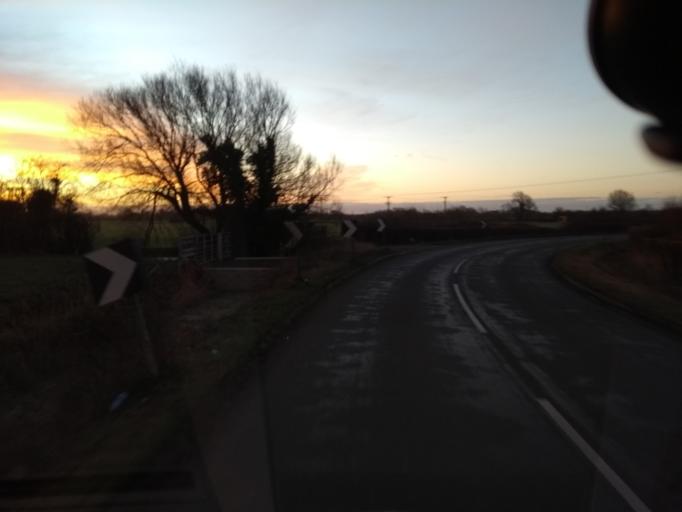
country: GB
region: England
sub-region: Somerset
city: Highbridge
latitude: 51.2276
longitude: -2.9434
